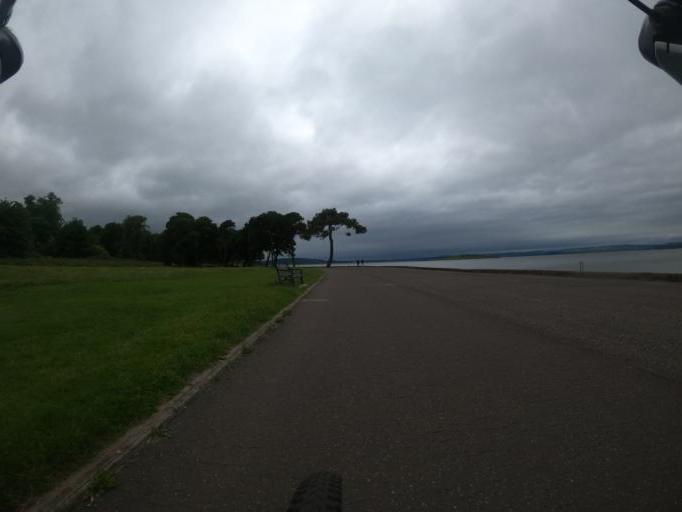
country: GB
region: Scotland
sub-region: Edinburgh
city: Colinton
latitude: 55.9795
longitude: -3.2666
